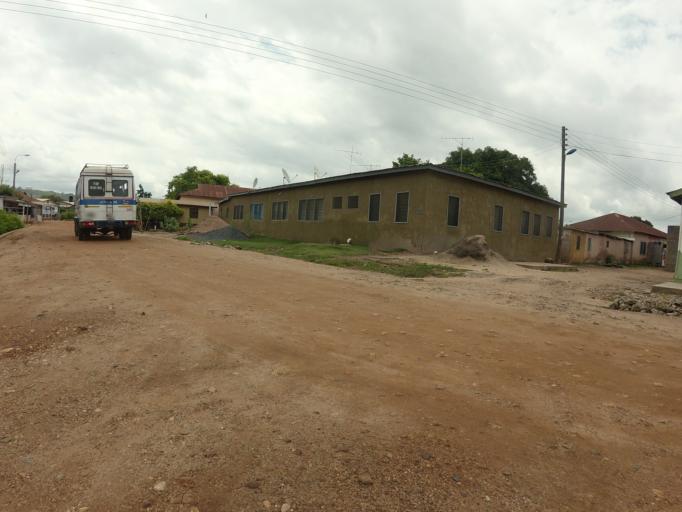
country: GH
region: Volta
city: Ho
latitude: 6.6015
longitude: 0.4697
